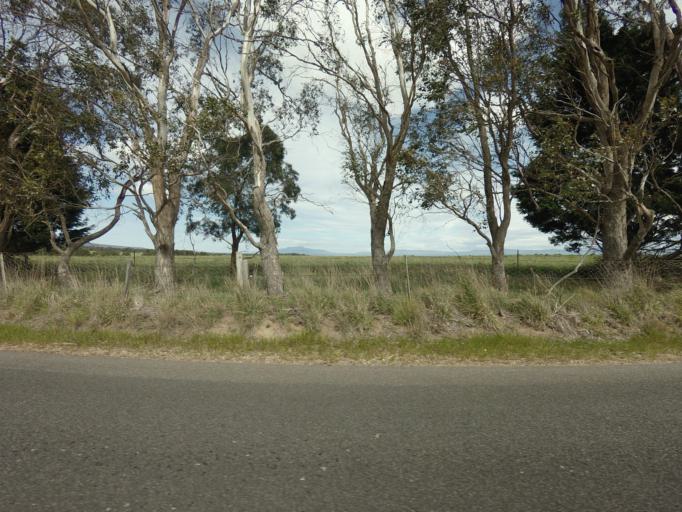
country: AU
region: Tasmania
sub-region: Northern Midlands
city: Longford
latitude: -41.6599
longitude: 147.1628
